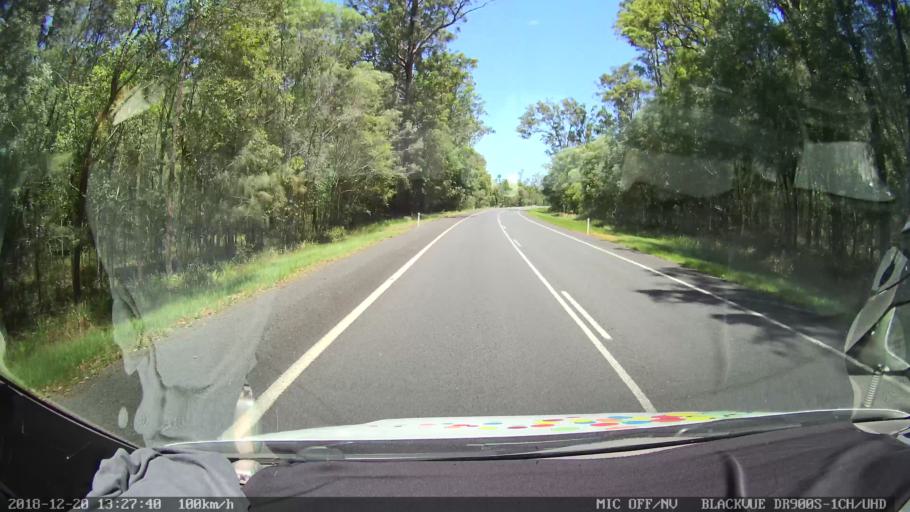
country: AU
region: New South Wales
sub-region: Clarence Valley
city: Gordon
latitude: -29.1633
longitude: 152.9928
